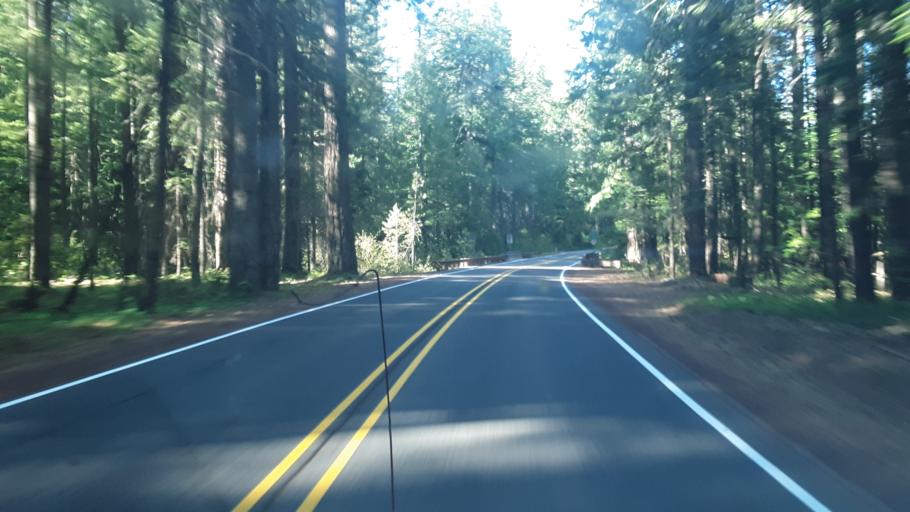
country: US
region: Oregon
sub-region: Jackson County
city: Shady Cove
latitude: 42.9286
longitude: -122.4232
